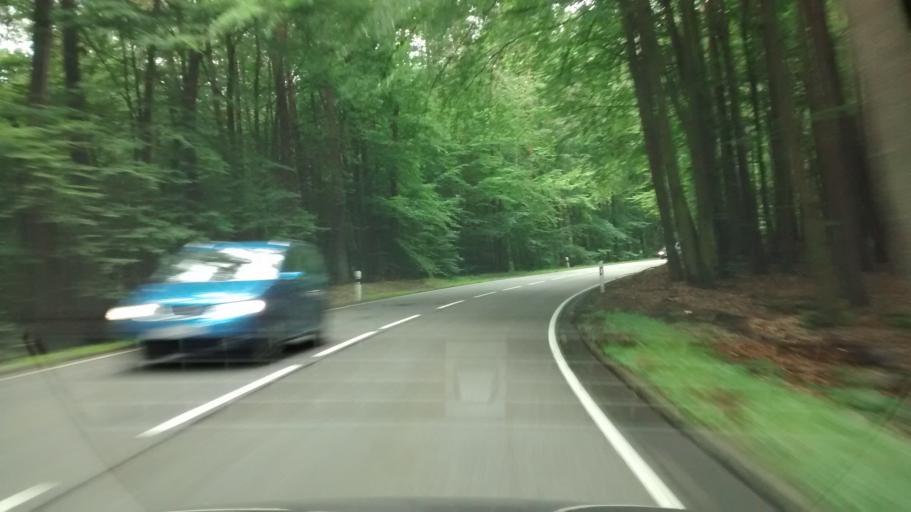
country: DE
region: Rheinland-Pfalz
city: Birkenhordt
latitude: 49.1139
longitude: 7.9107
